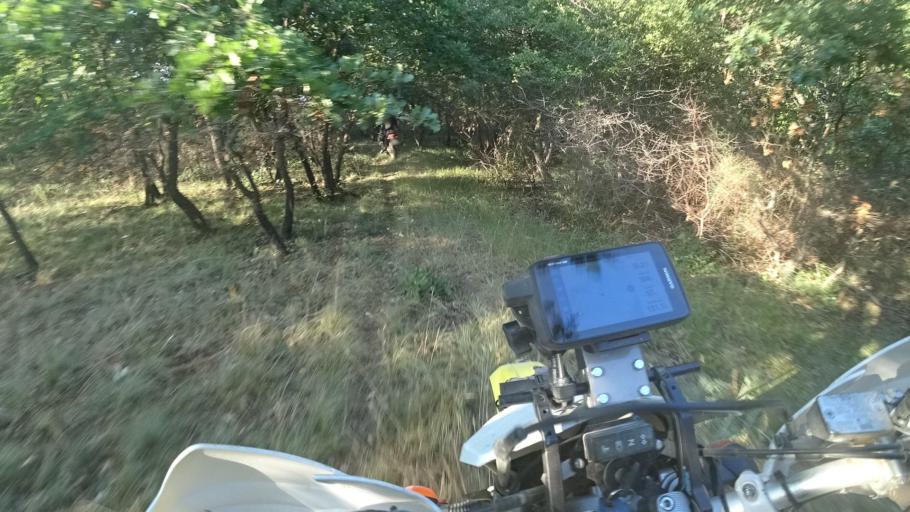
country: HR
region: Istarska
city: Marcana
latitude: 44.9512
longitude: 13.9099
